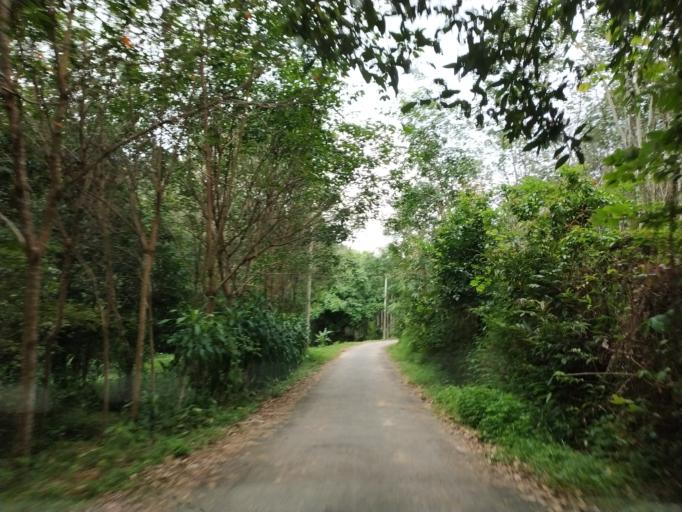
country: MM
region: Tanintharyi
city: Dawei
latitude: 13.8642
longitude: 98.2724
